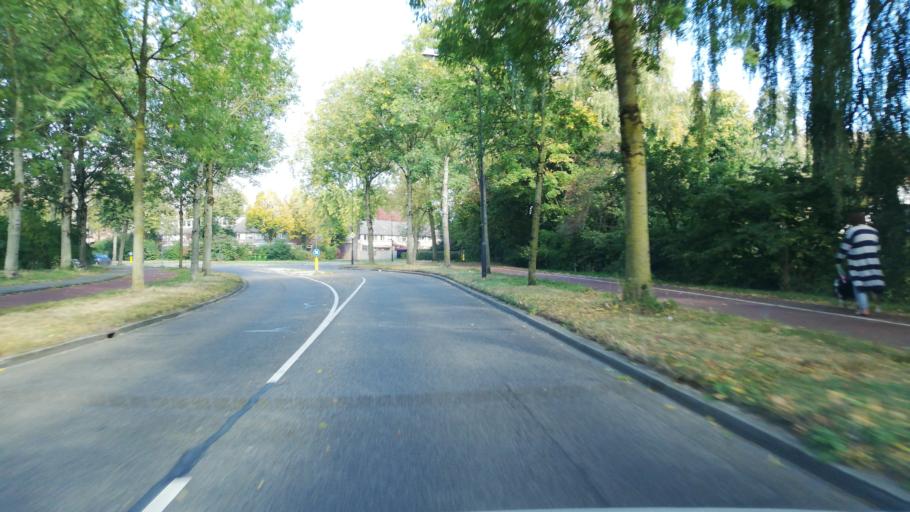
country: NL
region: Gelderland
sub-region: Gemeente Apeldoorn
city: Apeldoorn
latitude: 52.1933
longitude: 6.0111
